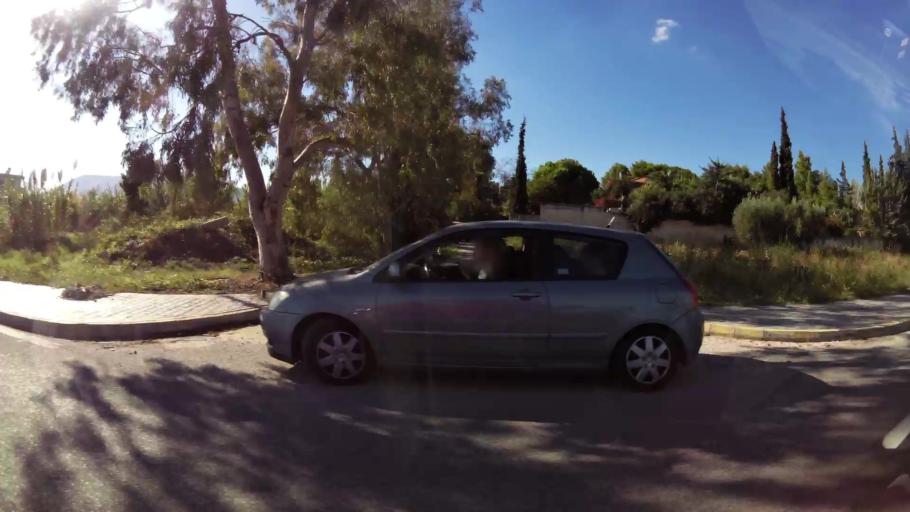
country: GR
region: Attica
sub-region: Nomarchia Anatolikis Attikis
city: Pallini
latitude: 38.0019
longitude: 23.8923
